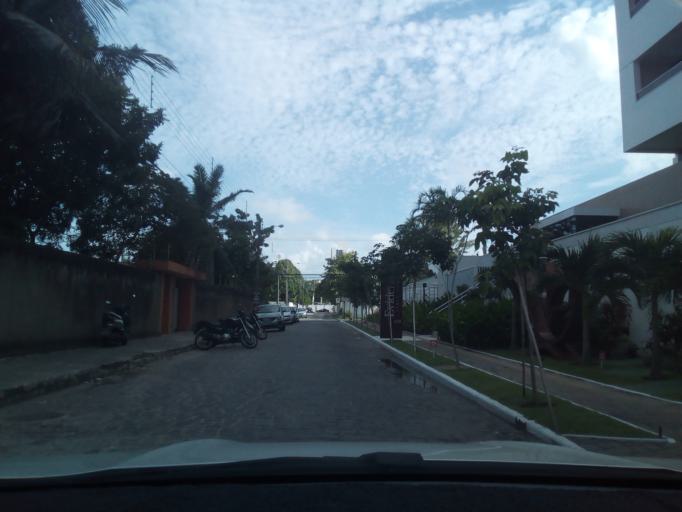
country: BR
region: Paraiba
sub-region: Joao Pessoa
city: Joao Pessoa
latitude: -7.1139
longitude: -34.8514
